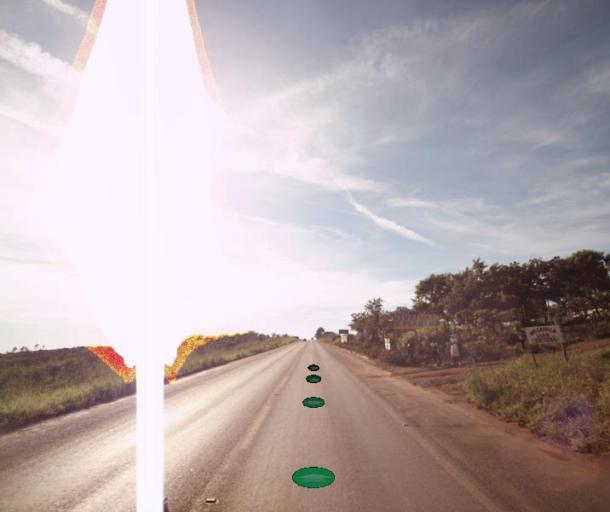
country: BR
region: Federal District
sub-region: Brasilia
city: Brasilia
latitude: -15.7376
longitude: -48.3943
